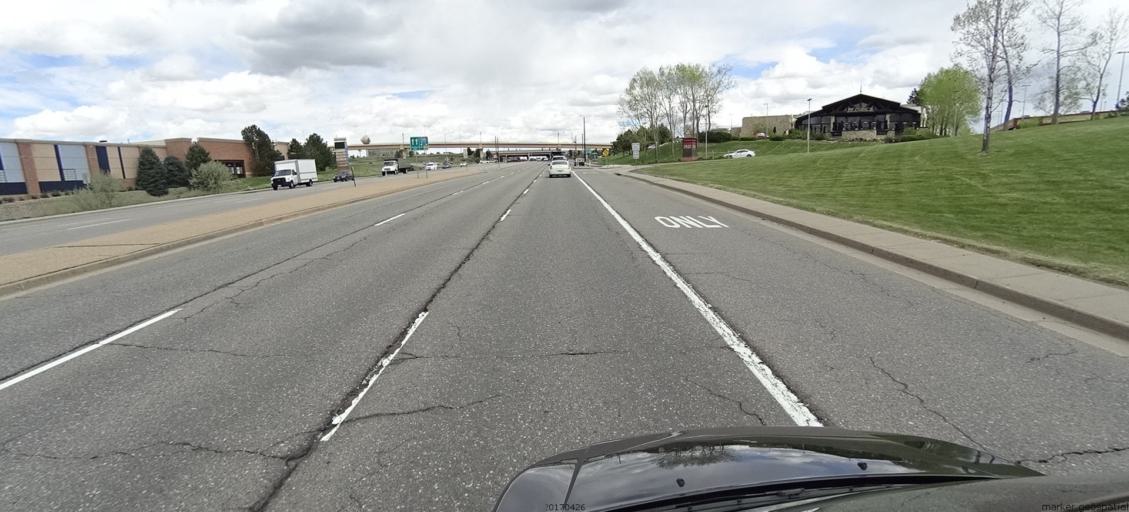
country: US
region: Colorado
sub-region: Arapahoe County
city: Centennial
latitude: 39.5659
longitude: -104.8775
